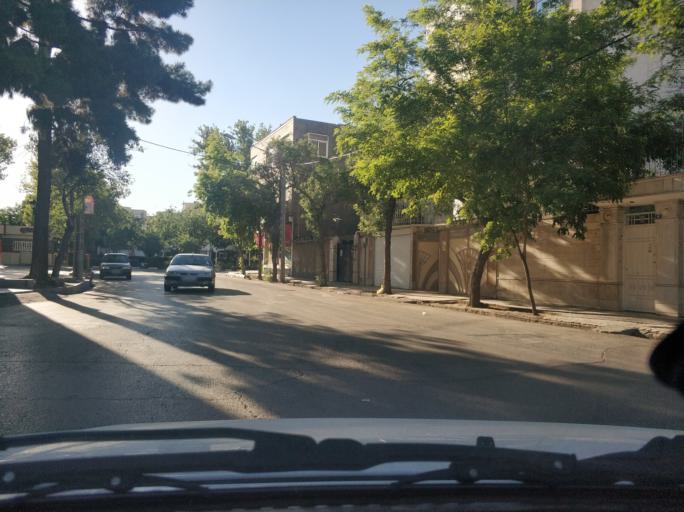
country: IR
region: Razavi Khorasan
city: Mashhad
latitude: 36.2763
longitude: 59.5936
